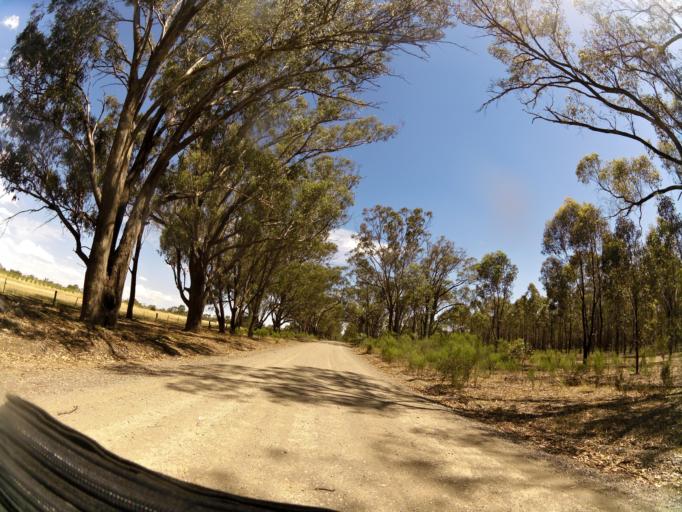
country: AU
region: Victoria
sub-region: Campaspe
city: Kyabram
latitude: -36.8180
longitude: 145.0804
